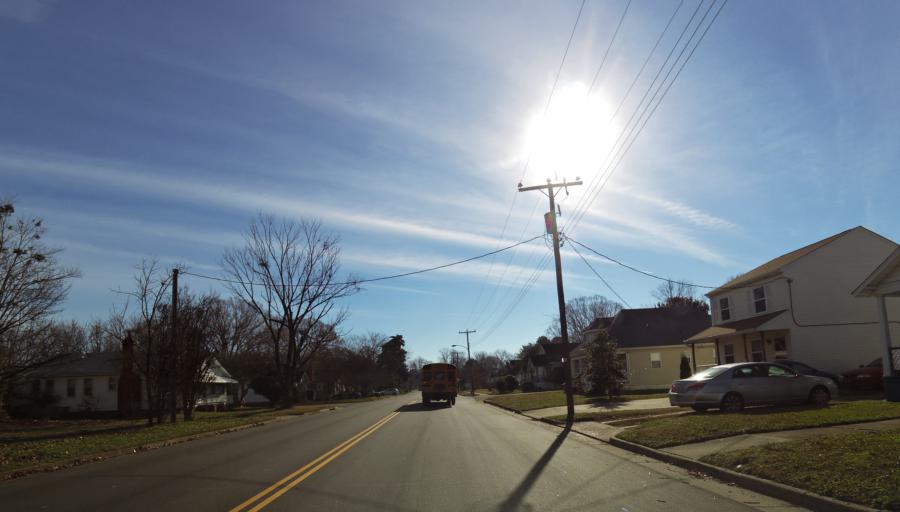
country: US
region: Virginia
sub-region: City of Hampton
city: Hampton
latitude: 37.0053
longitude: -76.3779
